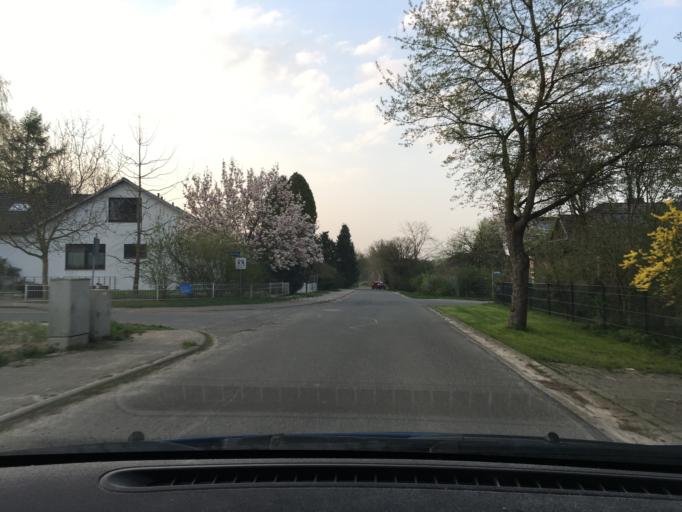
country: DE
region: Lower Saxony
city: Embsen
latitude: 53.1935
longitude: 10.3300
